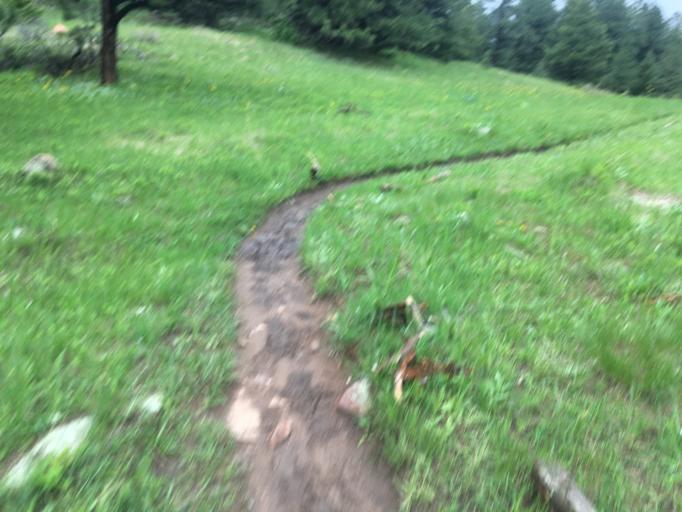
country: US
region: Colorado
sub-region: Boulder County
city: Boulder
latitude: 39.9193
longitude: -105.2767
